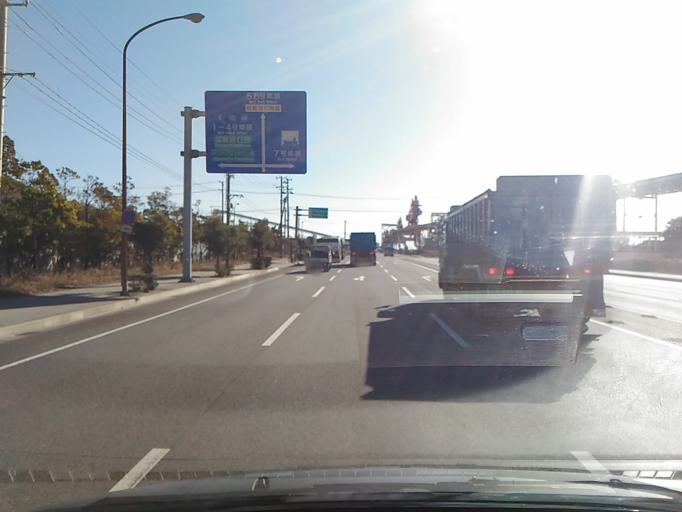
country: JP
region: Fukushima
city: Iwaki
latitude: 36.9377
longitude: 140.8795
